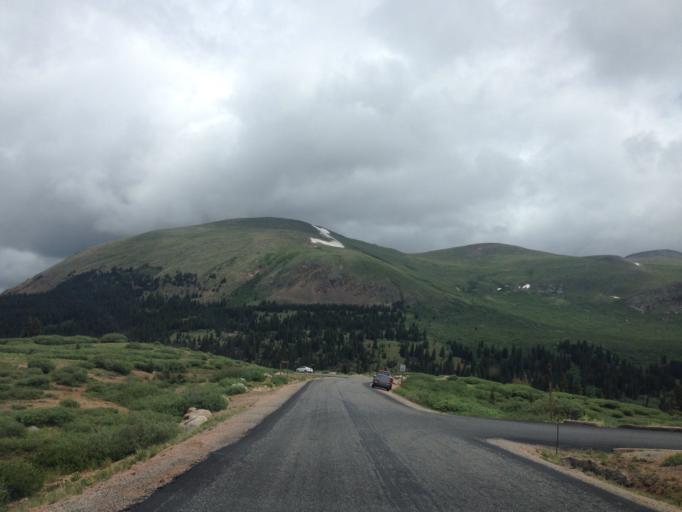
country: US
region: Colorado
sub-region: Clear Creek County
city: Georgetown
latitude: 39.5971
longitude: -105.7103
